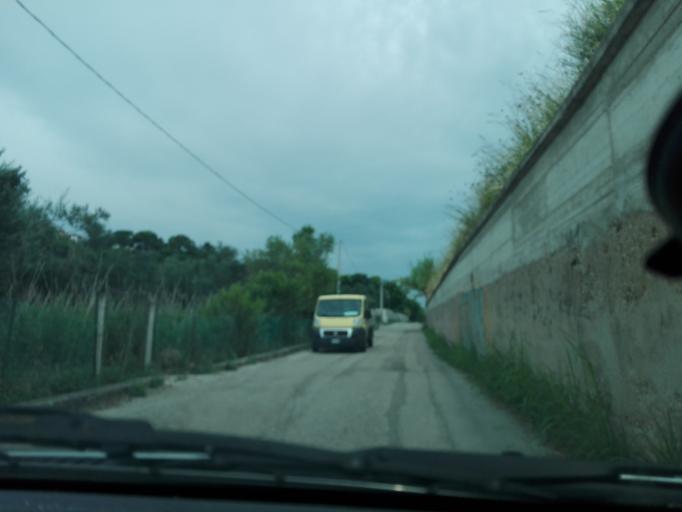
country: IT
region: Abruzzo
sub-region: Provincia di Pescara
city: Montesilvano Marina
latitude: 42.5010
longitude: 14.1638
